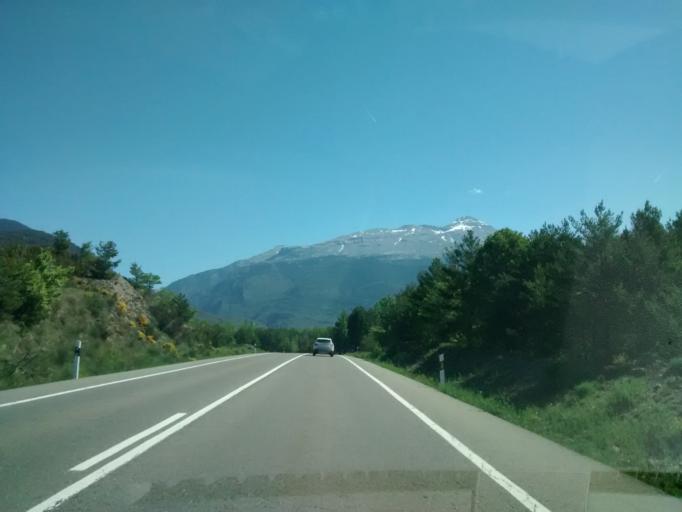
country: ES
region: Aragon
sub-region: Provincia de Huesca
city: Castiello de Jaca
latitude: 42.6564
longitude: -0.5566
